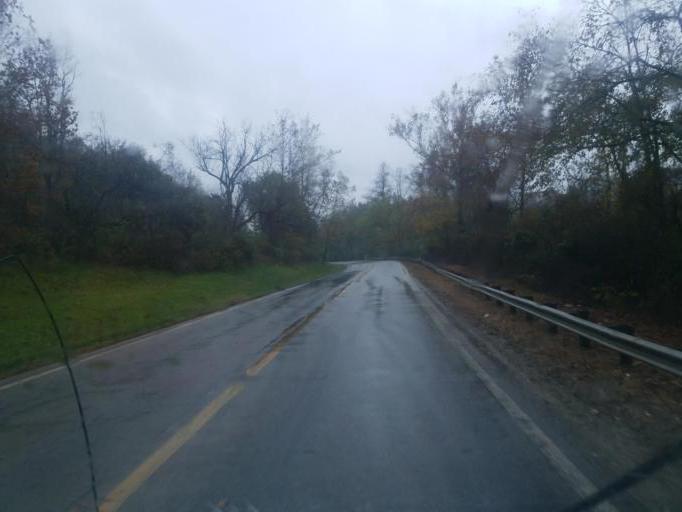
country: US
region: Ohio
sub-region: Morgan County
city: McConnelsville
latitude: 39.6299
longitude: -81.8358
